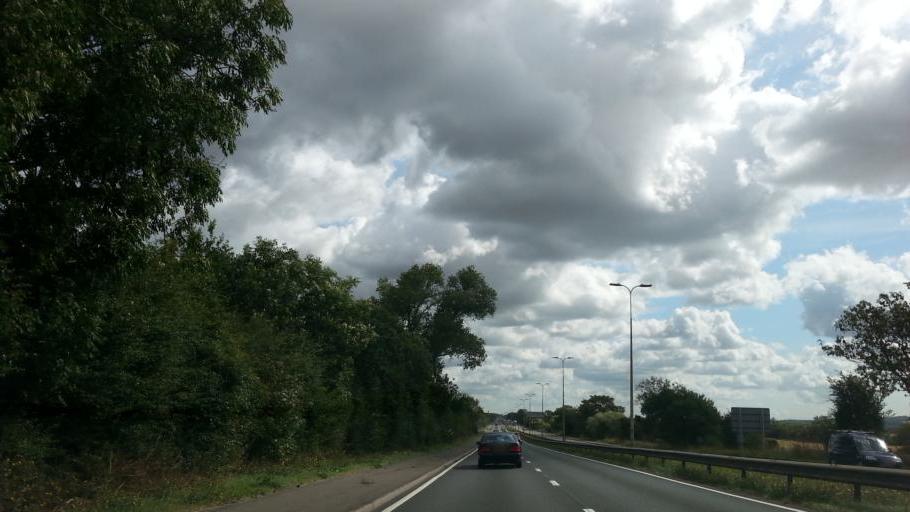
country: GB
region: England
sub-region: Essex
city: Brentwood
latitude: 51.5754
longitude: 0.3195
